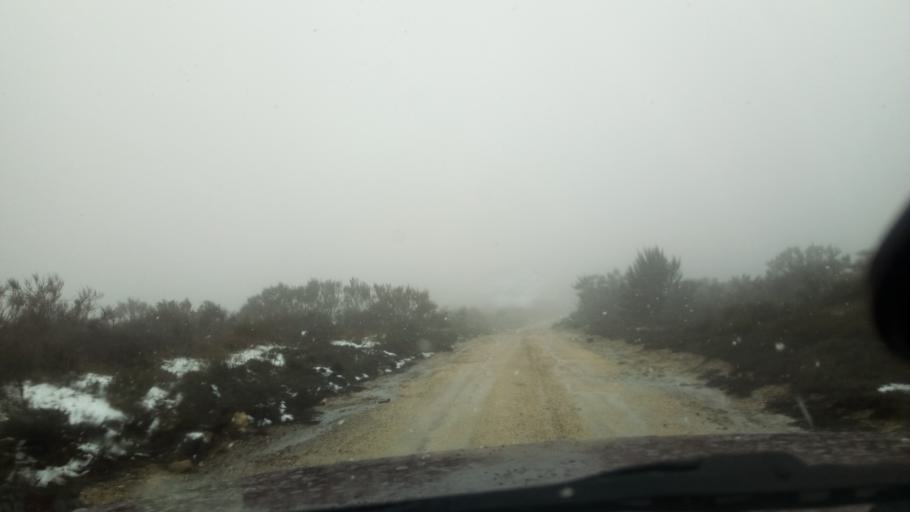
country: PT
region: Guarda
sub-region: Celorico da Beira
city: Celorico da Beira
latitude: 40.5308
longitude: -7.4458
